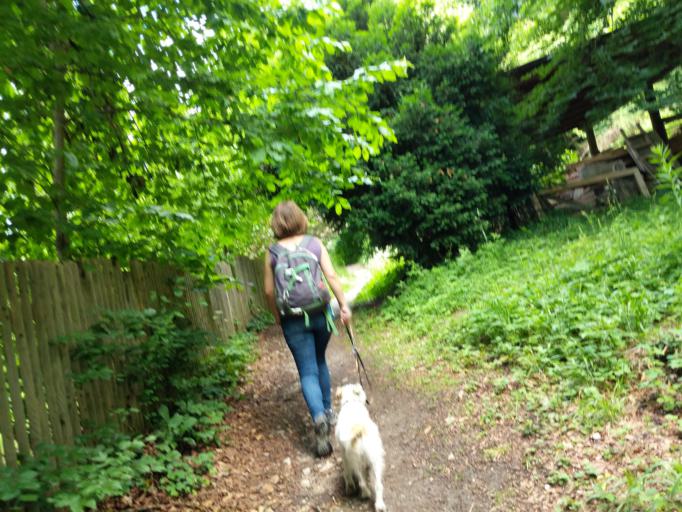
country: DE
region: Bavaria
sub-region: Upper Bavaria
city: Herrsching am Ammersee
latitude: 48.0042
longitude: 11.1848
